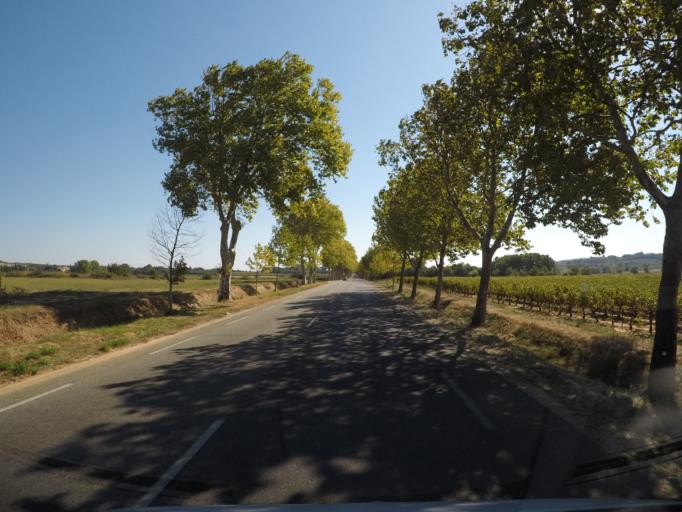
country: FR
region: Languedoc-Roussillon
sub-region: Departement du Gard
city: Ledenon
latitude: 43.9765
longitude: 4.4838
